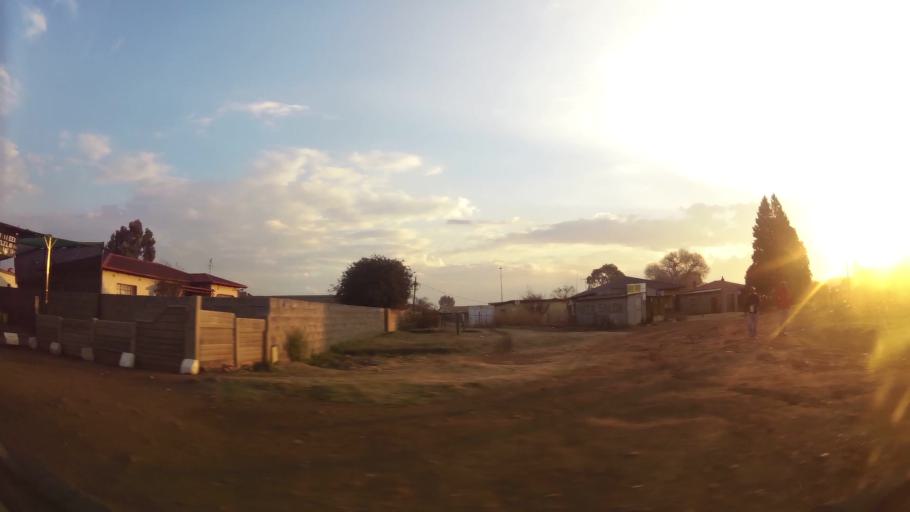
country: ZA
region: Gauteng
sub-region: City of Johannesburg Metropolitan Municipality
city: Orange Farm
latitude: -26.5413
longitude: 27.8844
